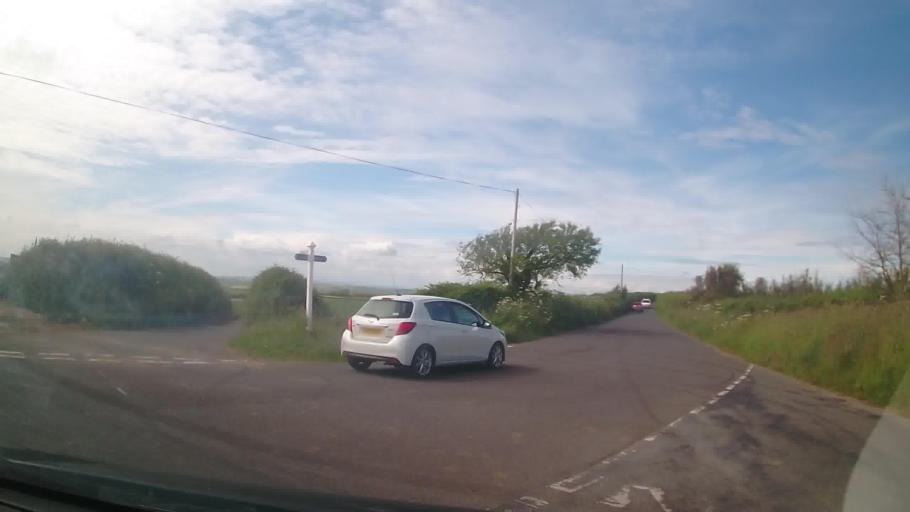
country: GB
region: England
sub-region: Devon
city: Salcombe
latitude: 50.2497
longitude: -3.6822
